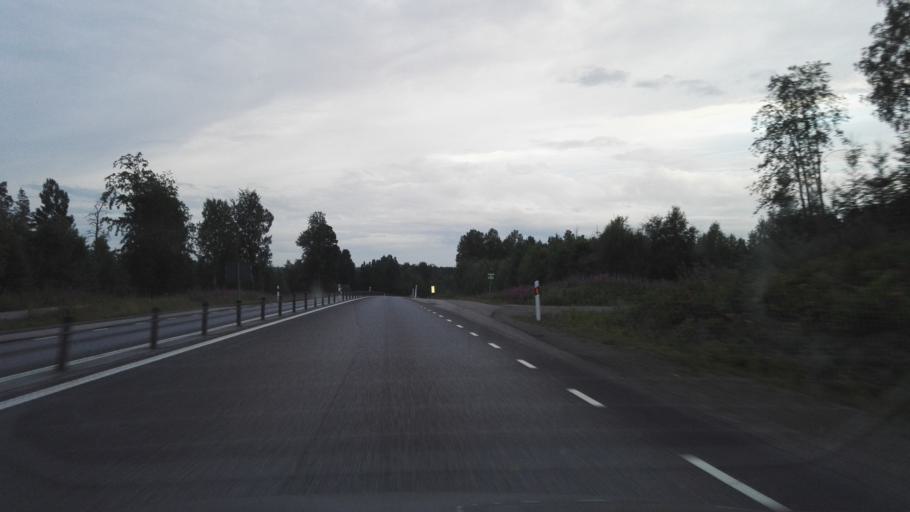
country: SE
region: Kronoberg
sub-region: Vaxjo Kommun
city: Vaexjoe
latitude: 56.9333
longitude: 14.8665
